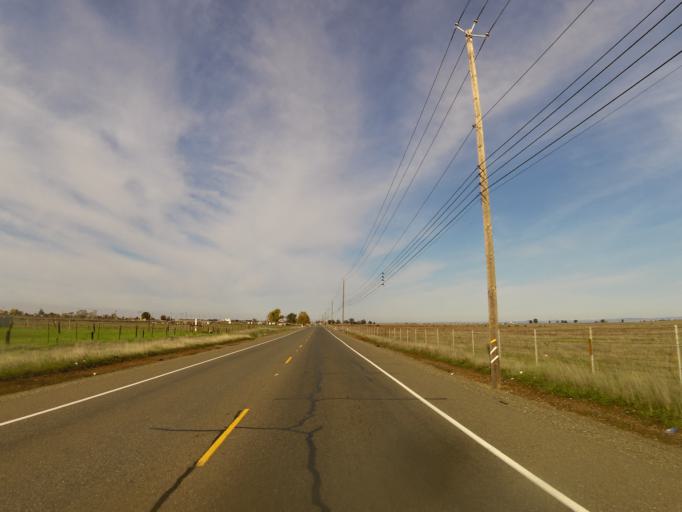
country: US
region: California
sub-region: Sacramento County
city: Wilton
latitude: 38.4909
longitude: -121.2423
